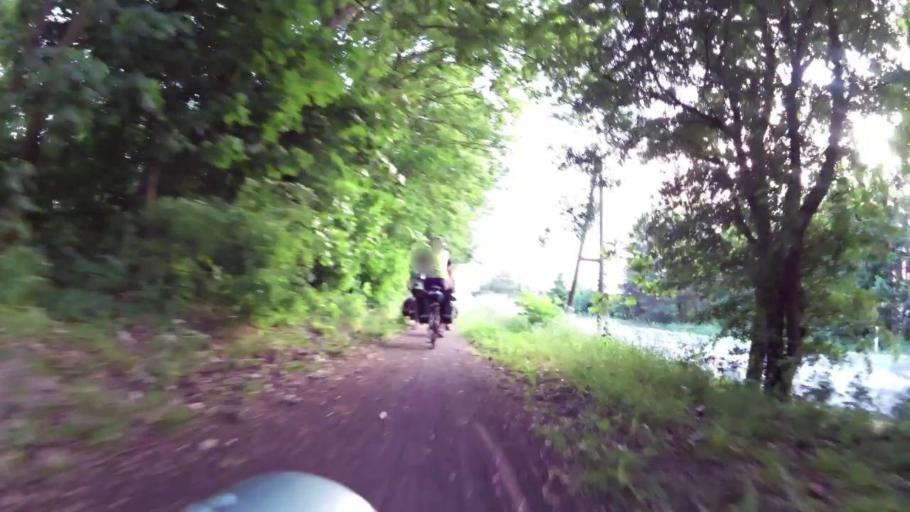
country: PL
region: Kujawsko-Pomorskie
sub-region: Powiat bydgoski
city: Dabrowa Chelminska
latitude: 53.1602
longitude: 18.2412
